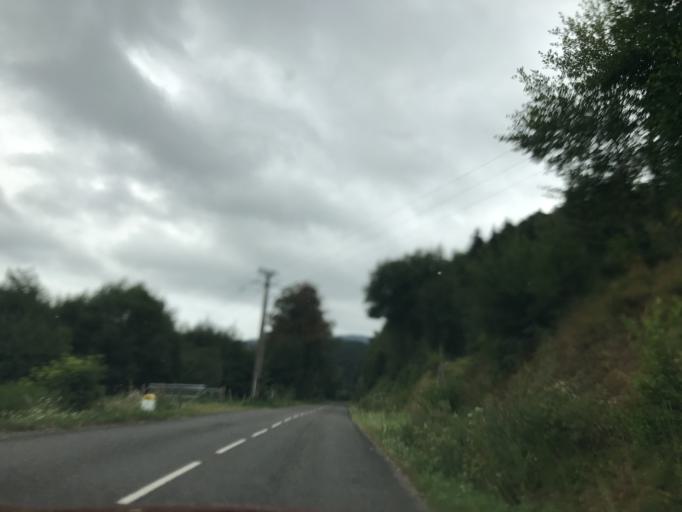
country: FR
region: Rhone-Alpes
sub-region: Departement de la Loire
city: Sail-sous-Couzan
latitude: 45.7015
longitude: 3.8520
